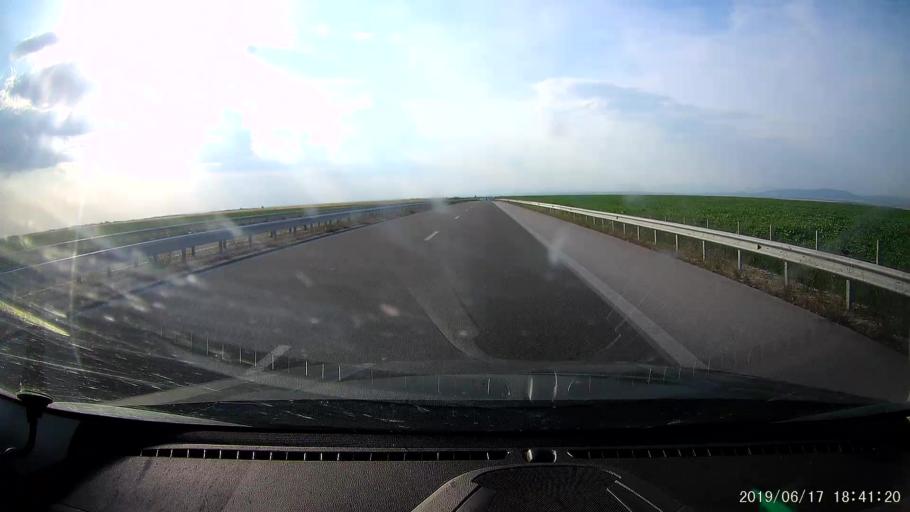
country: BG
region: Stara Zagora
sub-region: Obshtina Chirpan
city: Chirpan
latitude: 42.1703
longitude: 25.2577
